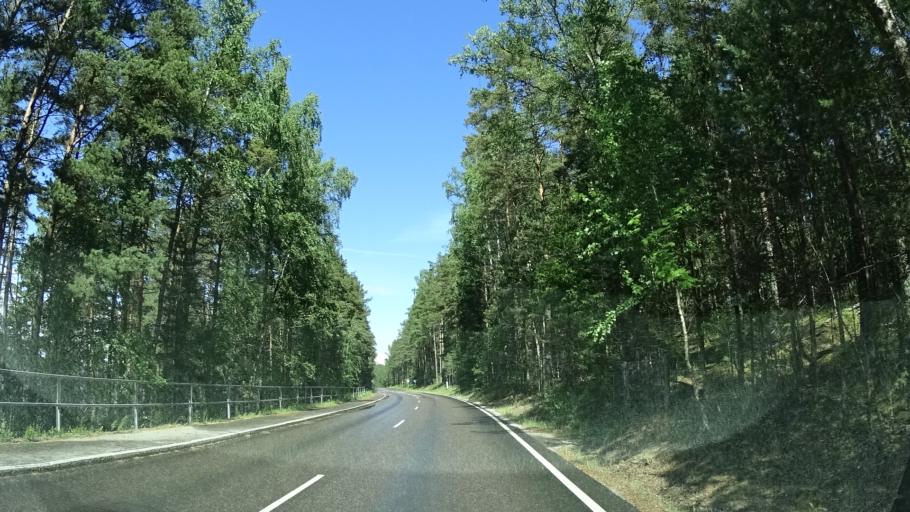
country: FI
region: Paijanne Tavastia
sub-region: Lahti
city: Asikkala
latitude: 61.2690
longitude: 25.5232
